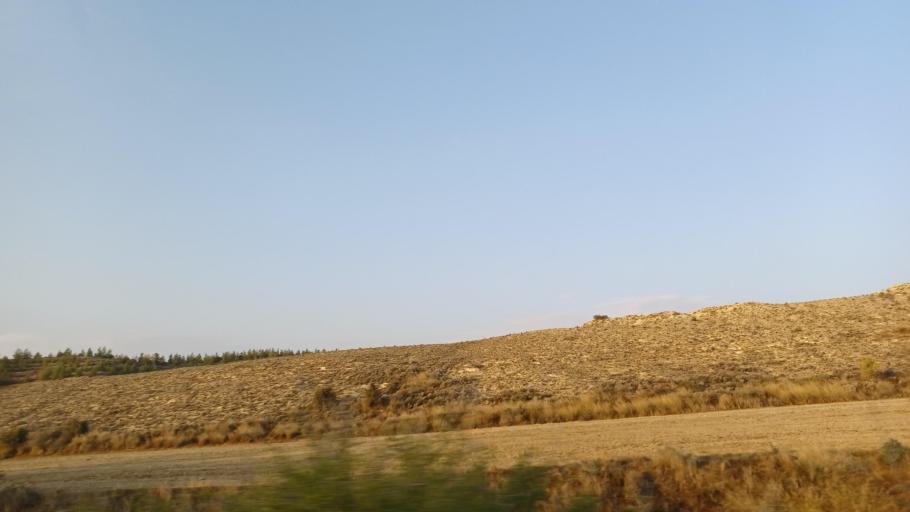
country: CY
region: Larnaka
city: Athienou
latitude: 35.0048
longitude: 33.5245
